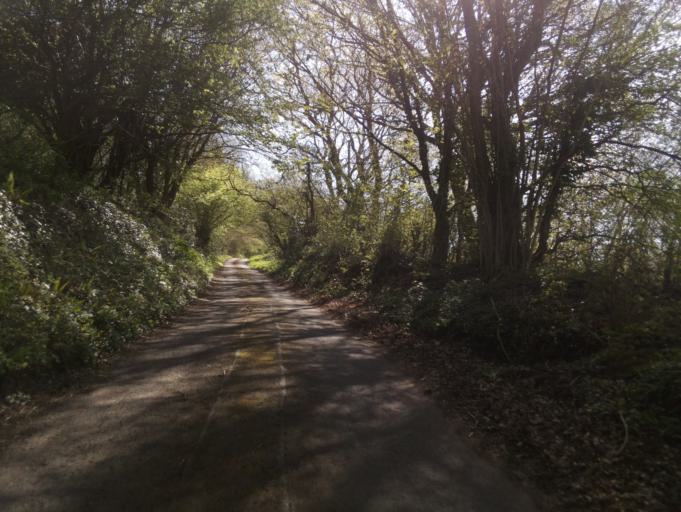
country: GB
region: Wales
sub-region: Monmouthshire
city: Llangwm
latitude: 51.6856
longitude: -2.8137
